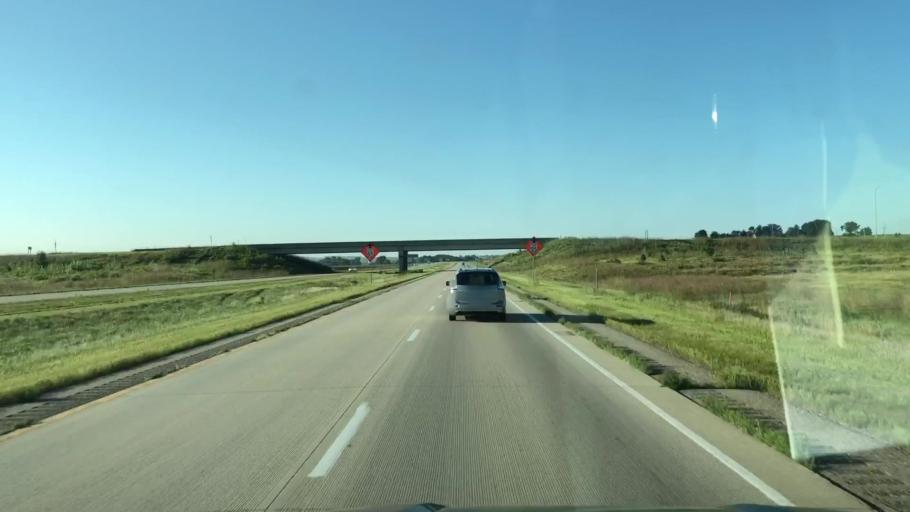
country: US
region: Iowa
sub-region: Plymouth County
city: Le Mars
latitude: 42.7661
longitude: -96.2095
